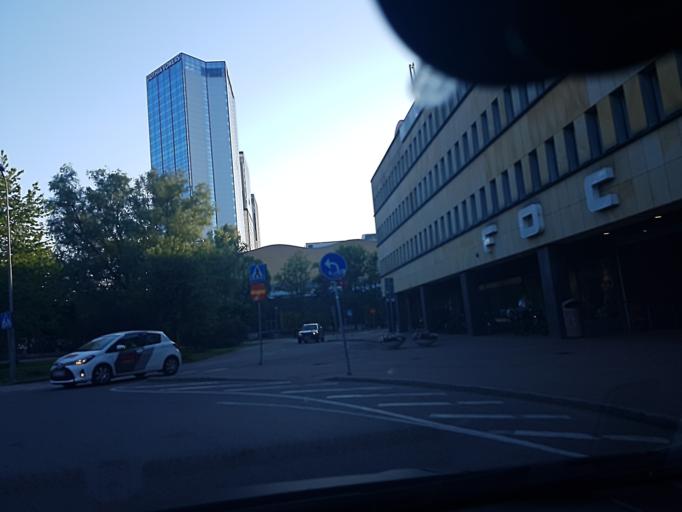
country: SE
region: Vaestra Goetaland
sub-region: Goteborg
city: Goeteborg
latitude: 57.6981
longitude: 11.9934
